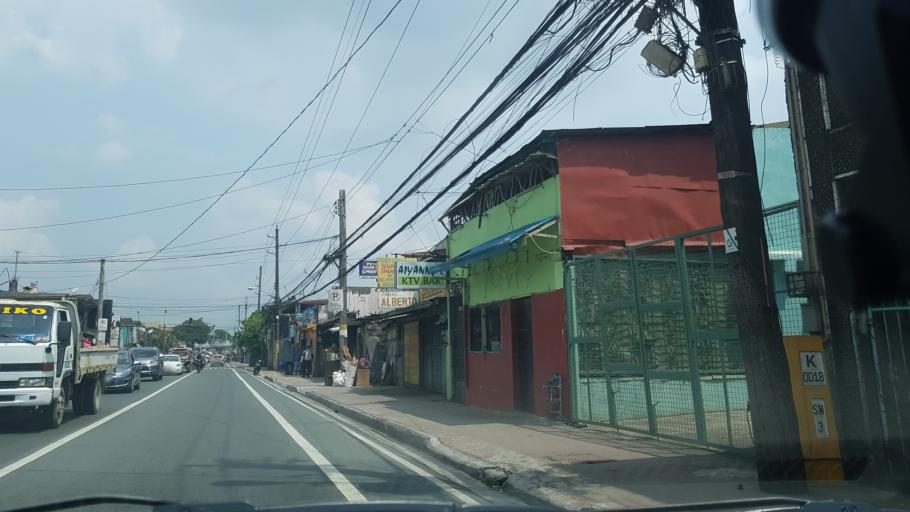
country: PH
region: Metro Manila
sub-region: Marikina
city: Calumpang
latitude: 14.6548
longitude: 121.1033
